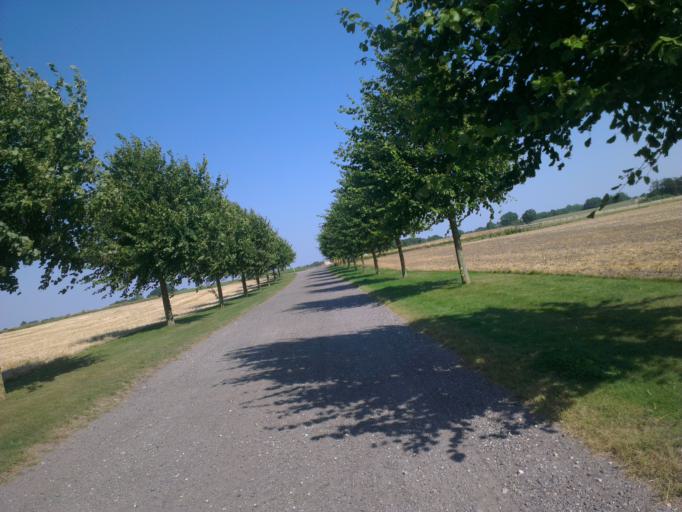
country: DK
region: Capital Region
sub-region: Frederikssund Kommune
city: Skibby
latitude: 55.7666
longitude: 11.9465
